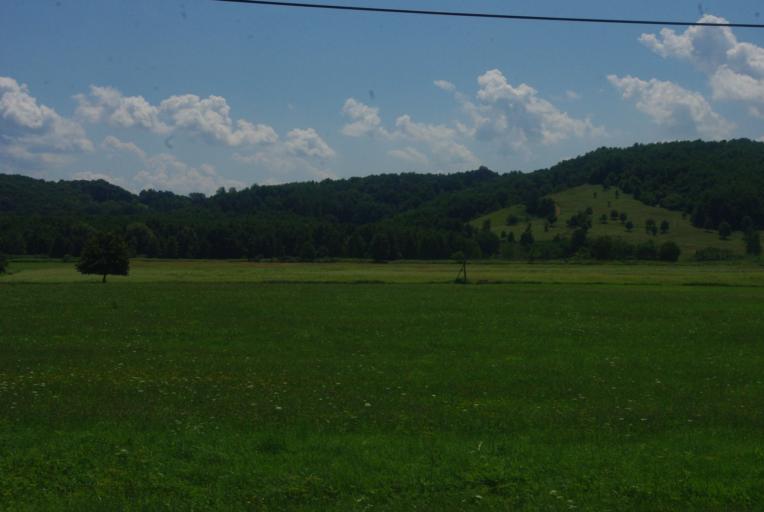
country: HU
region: Zala
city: Letenye
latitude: 46.5670
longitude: 16.6911
